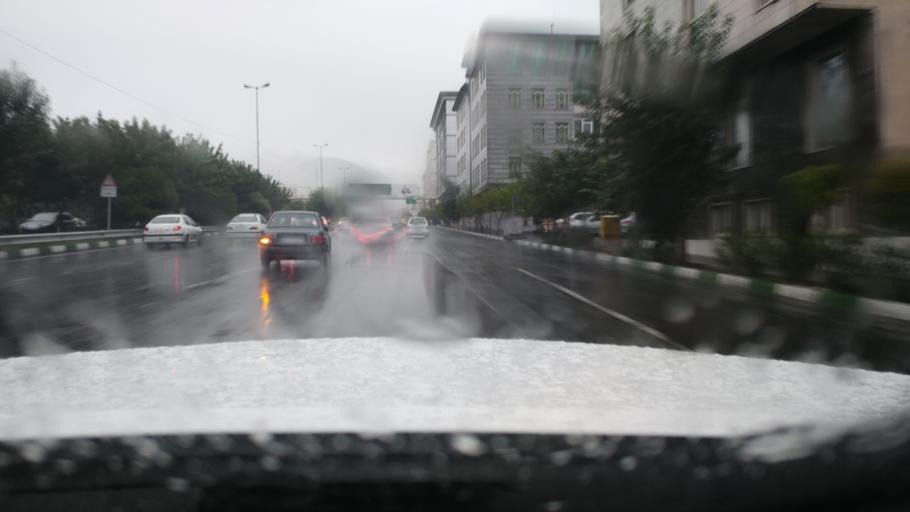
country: IR
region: Tehran
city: Tehran
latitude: 35.7271
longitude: 51.3100
